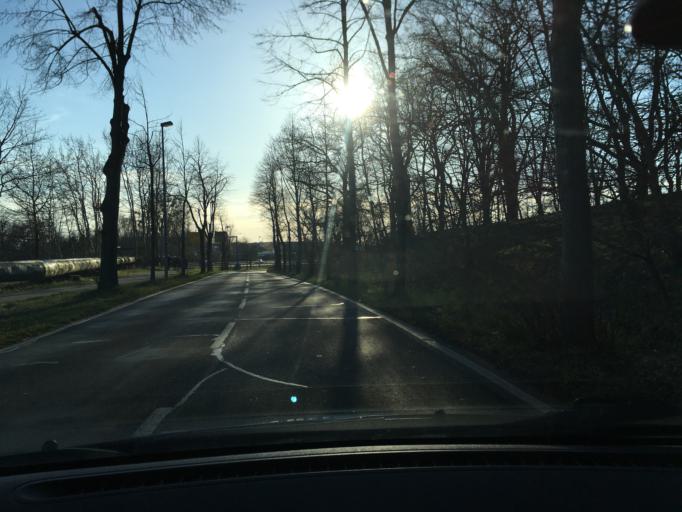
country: DE
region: Mecklenburg-Vorpommern
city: Feldstadt
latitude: 53.5937
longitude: 11.4102
